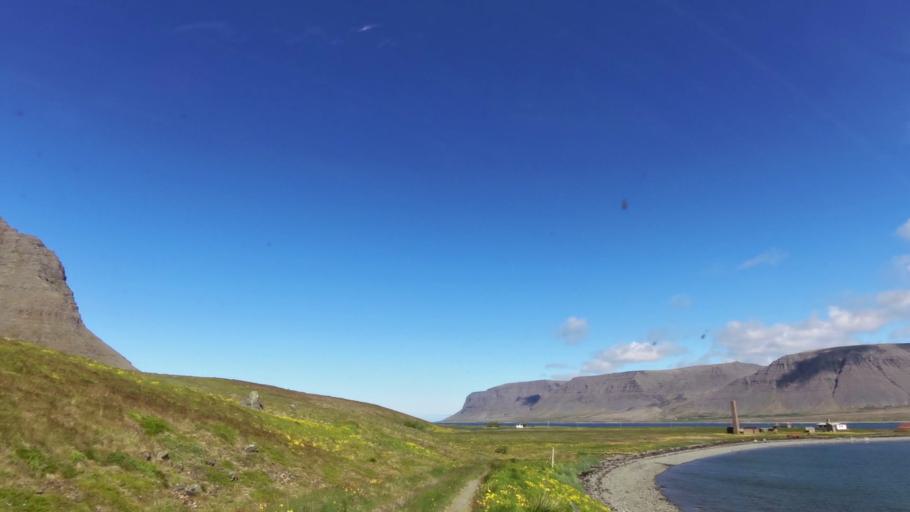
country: IS
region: West
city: Olafsvik
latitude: 65.6366
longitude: -23.9307
